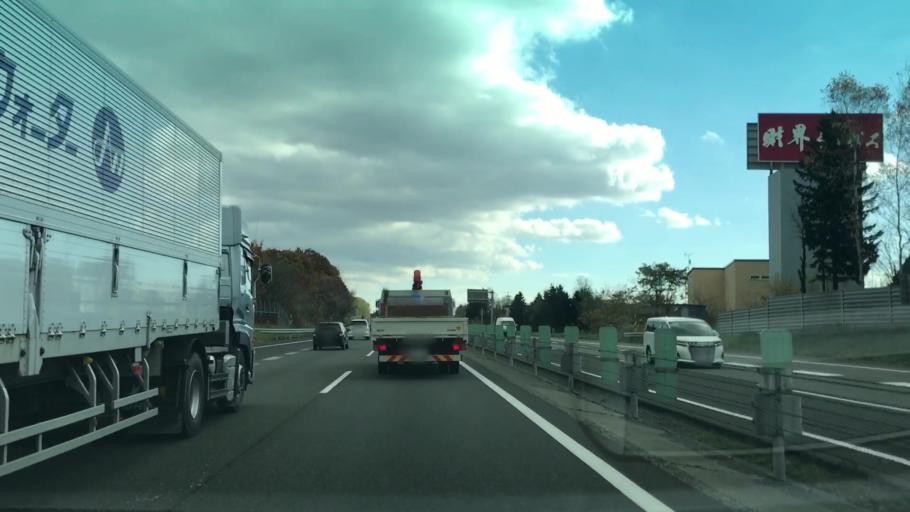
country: JP
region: Hokkaido
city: Kitahiroshima
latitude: 42.9753
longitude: 141.4804
